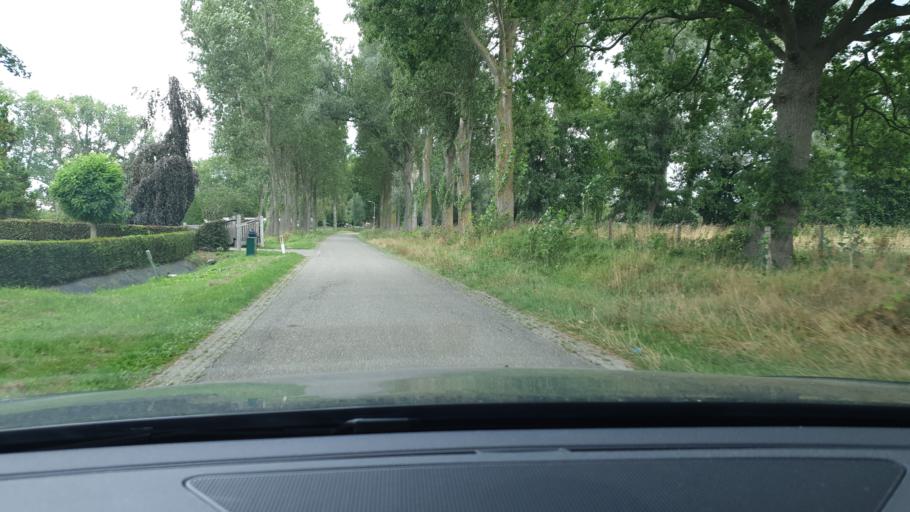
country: NL
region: North Brabant
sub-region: Gemeente Son en Breugel
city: Son
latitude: 51.4909
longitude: 5.5068
